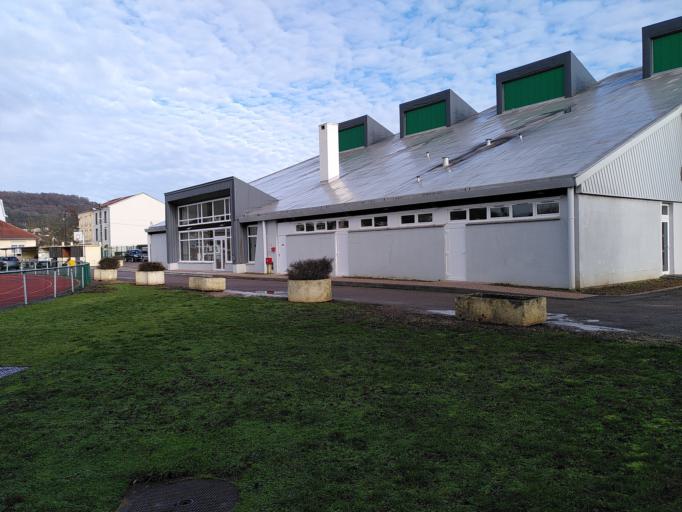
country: FR
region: Lorraine
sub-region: Departement de Meurthe-et-Moselle
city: Frouard
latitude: 48.7636
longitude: 6.1290
